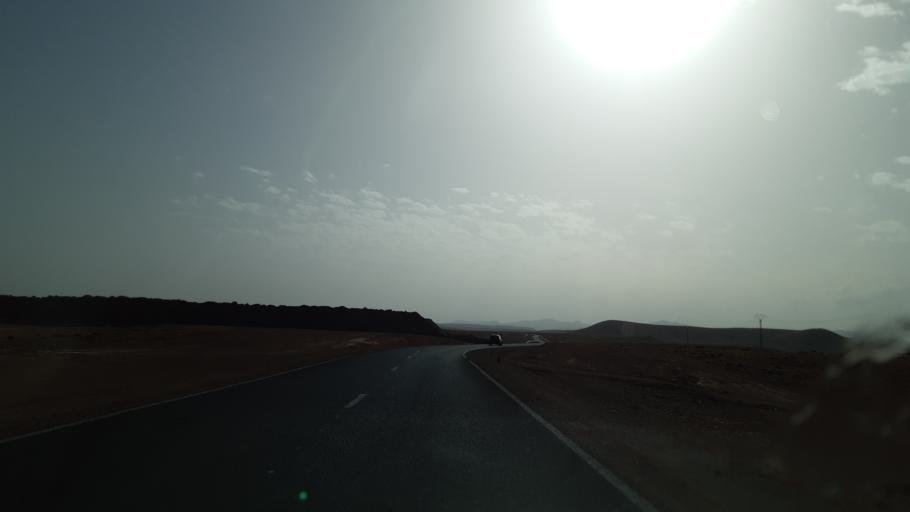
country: MA
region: Meknes-Tafilalet
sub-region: Khenifra
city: Itzer
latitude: 32.8639
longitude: -4.9255
